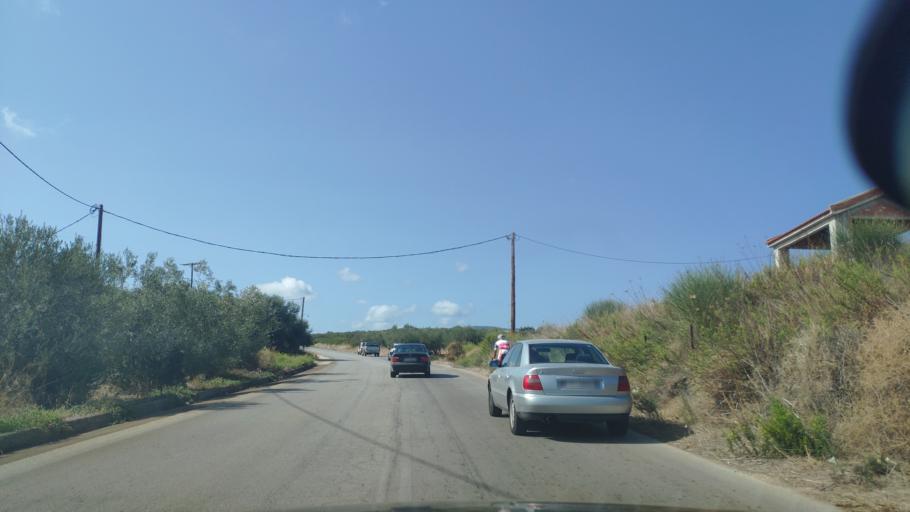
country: GR
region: Peloponnese
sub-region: Nomos Korinthias
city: Moulki
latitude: 37.9954
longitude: 22.7026
